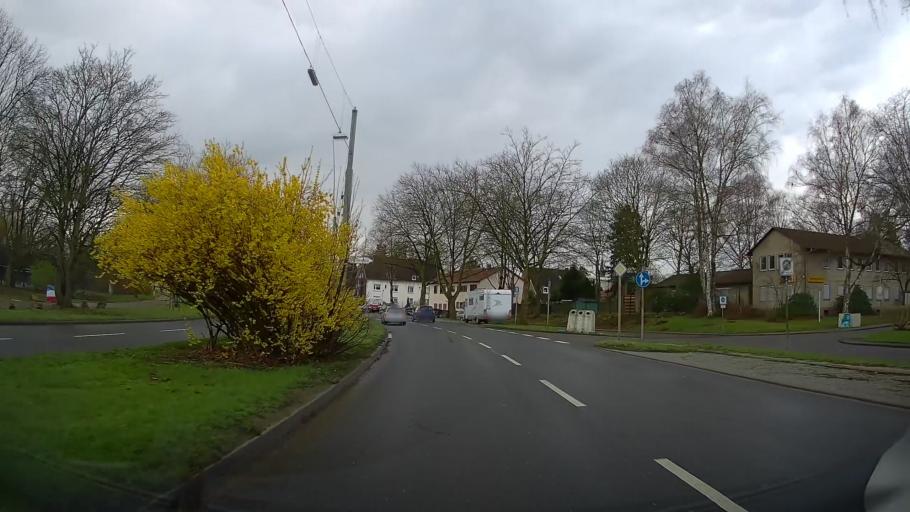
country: DE
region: North Rhine-Westphalia
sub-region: Regierungsbezirk Arnsberg
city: Herne
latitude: 51.5509
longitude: 7.2075
